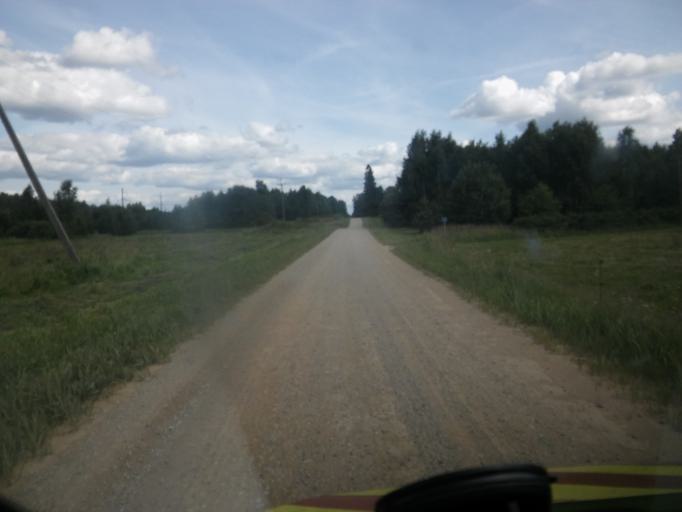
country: EE
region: Viljandimaa
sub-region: Karksi vald
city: Karksi-Nuia
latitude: 58.0871
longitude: 25.4944
